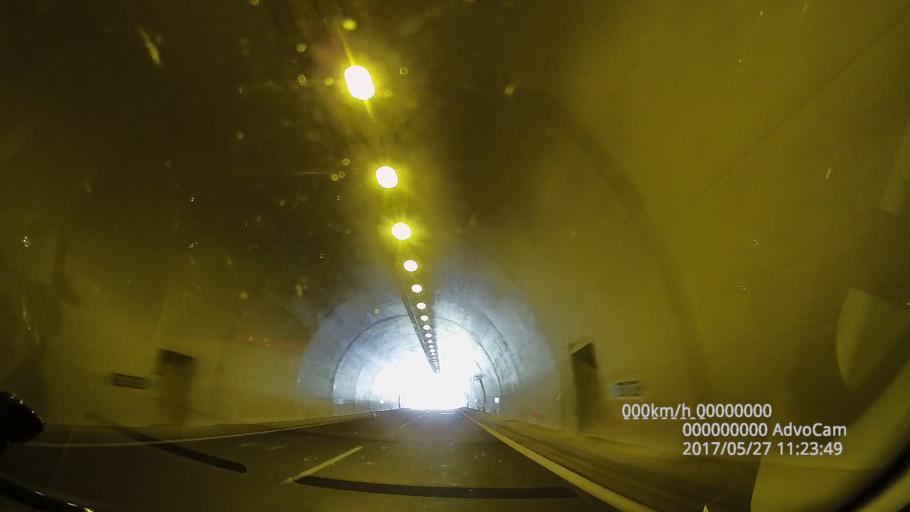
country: GR
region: Central Macedonia
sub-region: Nomos Thessalonikis
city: Xilopolis
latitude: 40.9787
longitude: 23.1835
